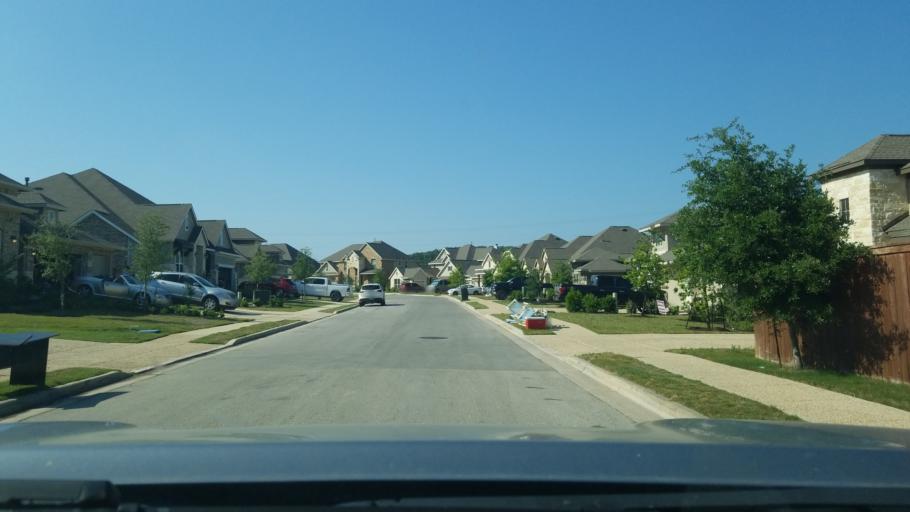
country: US
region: Texas
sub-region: Comal County
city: Bulverde
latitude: 29.7742
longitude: -98.4210
